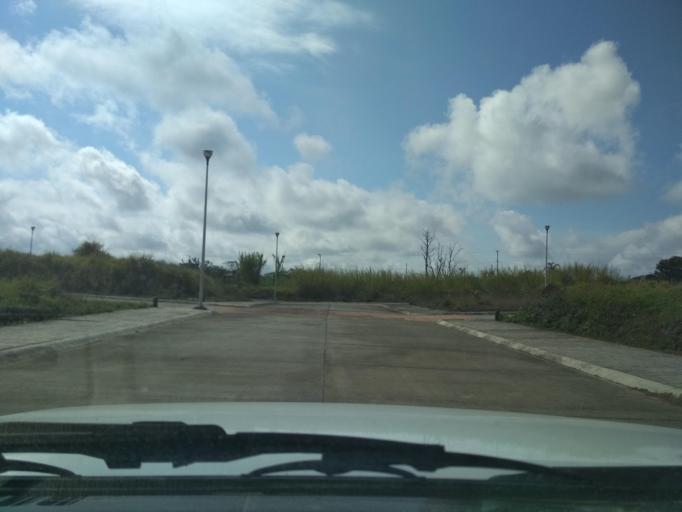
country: MX
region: Veracruz
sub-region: Emiliano Zapata
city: Jacarandas
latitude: 19.4983
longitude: -96.8401
